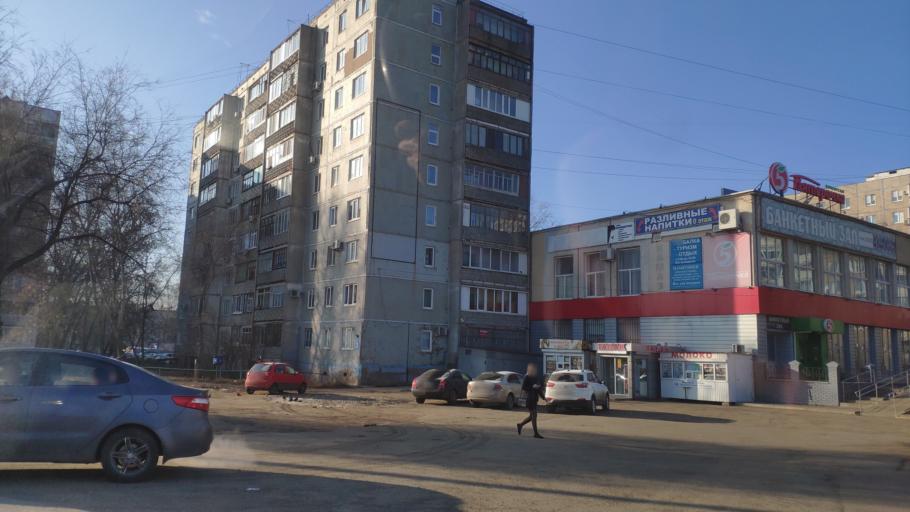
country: RU
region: Orenburg
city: Prigorodnyy
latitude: 51.7787
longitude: 55.1900
